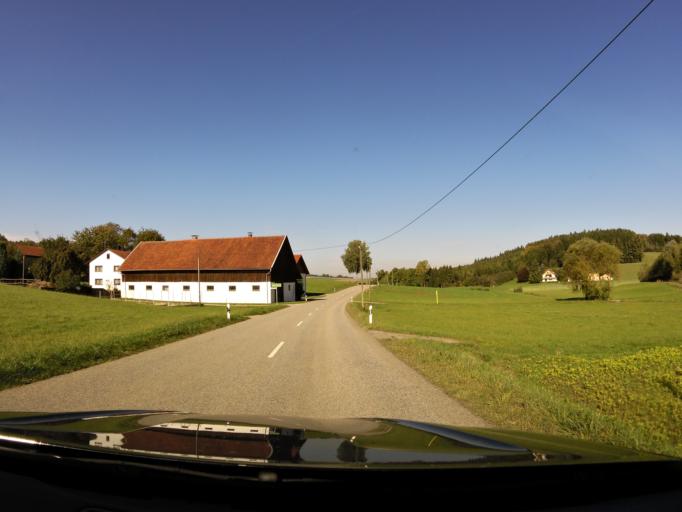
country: DE
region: Bavaria
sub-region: Lower Bavaria
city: Tiefenbach
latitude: 48.4825
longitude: 12.1127
